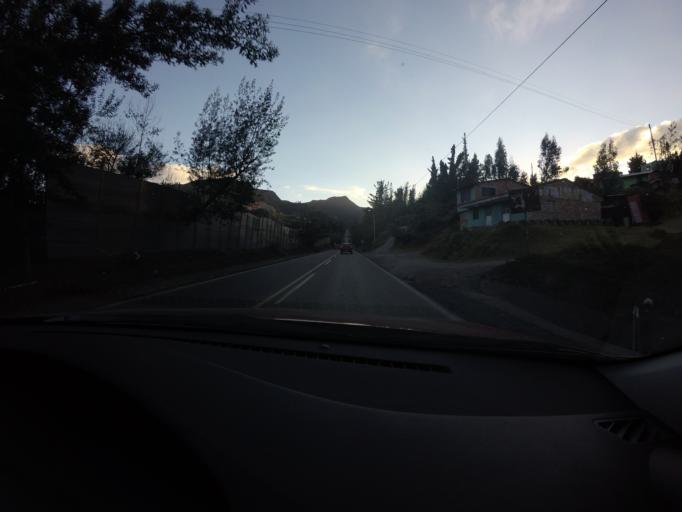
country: CO
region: Cundinamarca
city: Sutatausa
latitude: 5.2254
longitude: -73.8584
